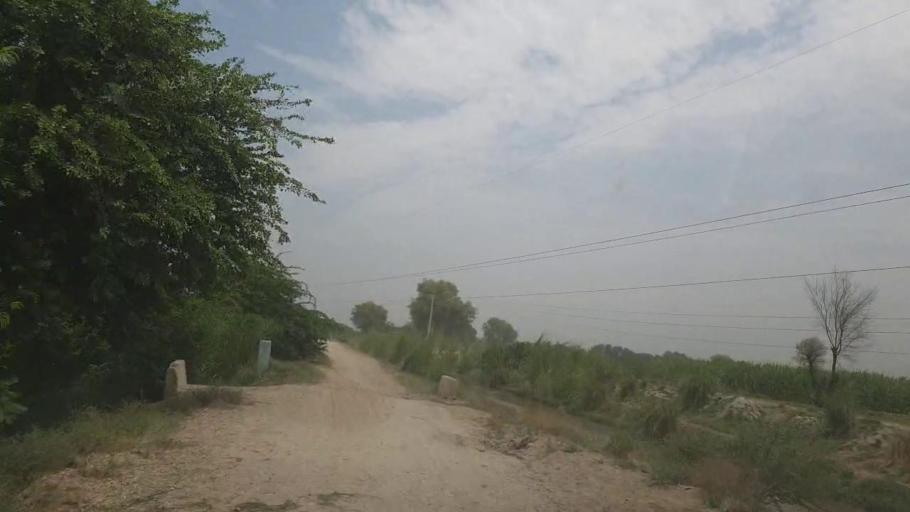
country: PK
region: Sindh
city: Kot Diji
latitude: 27.4330
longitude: 68.6613
